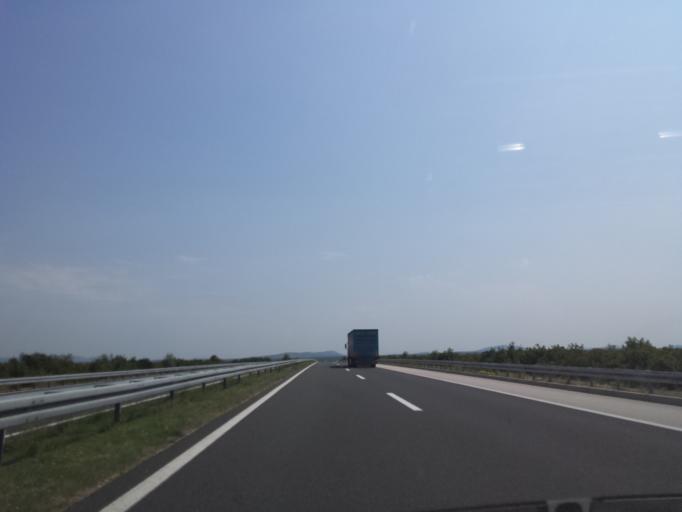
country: HR
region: Zadarska
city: Benkovac
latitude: 44.0028
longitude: 15.5995
